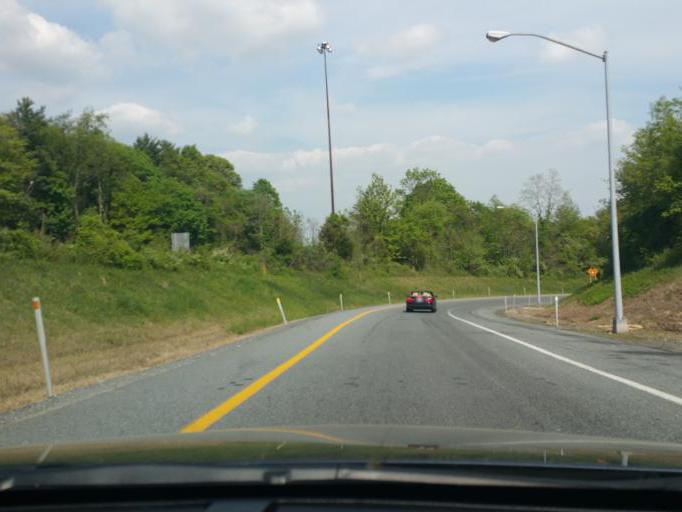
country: US
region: Maryland
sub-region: Cecil County
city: Perryville
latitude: 39.5957
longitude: -76.0665
